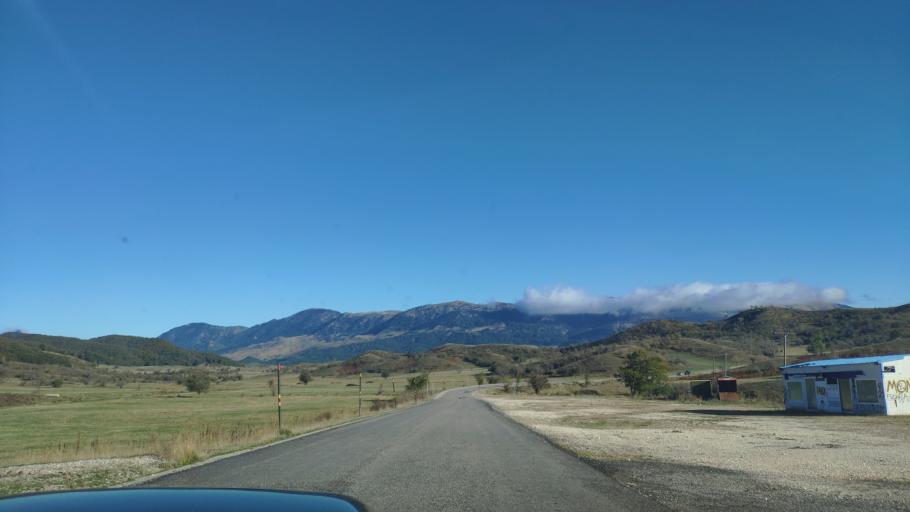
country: GR
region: Epirus
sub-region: Nomos Ioanninon
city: Metsovo
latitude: 39.7852
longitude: 21.1589
